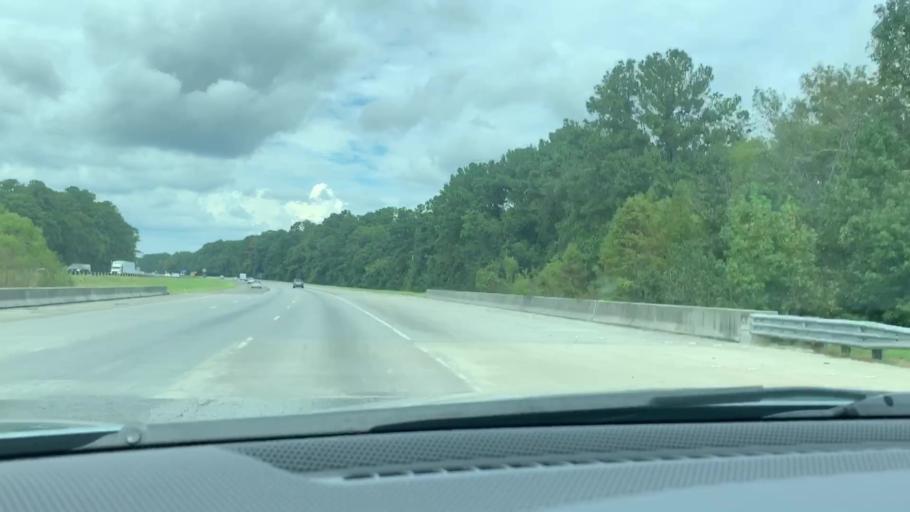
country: US
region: Georgia
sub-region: Bryan County
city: Richmond Hill
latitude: 31.9011
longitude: -81.3215
